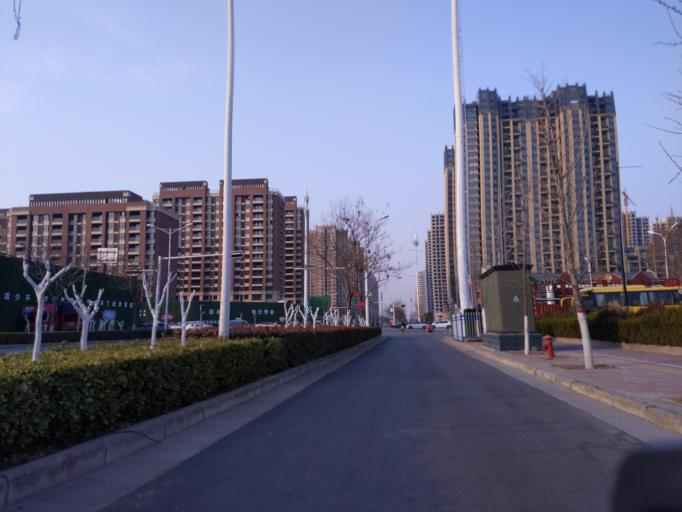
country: CN
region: Henan Sheng
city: Puyang
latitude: 35.7859
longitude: 115.0151
